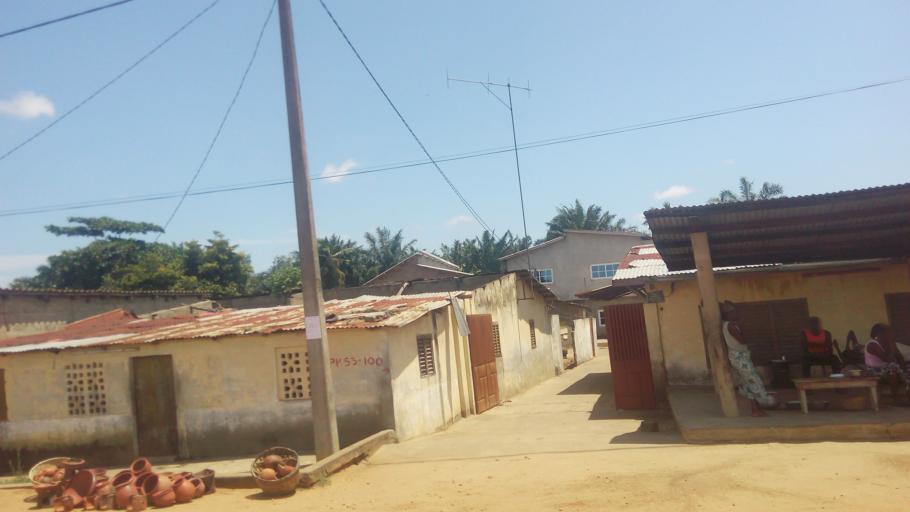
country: BJ
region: Mono
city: Come
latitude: 6.4019
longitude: 1.9091
